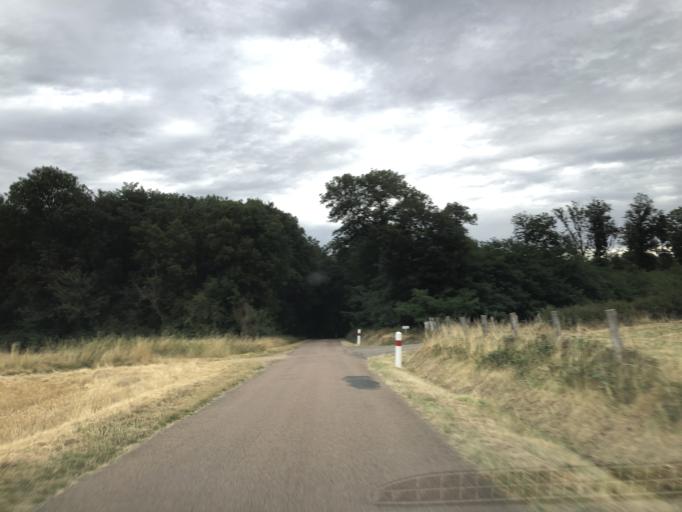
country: FR
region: Bourgogne
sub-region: Departement de l'Yonne
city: Aillant-sur-Tholon
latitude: 47.9047
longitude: 3.3086
